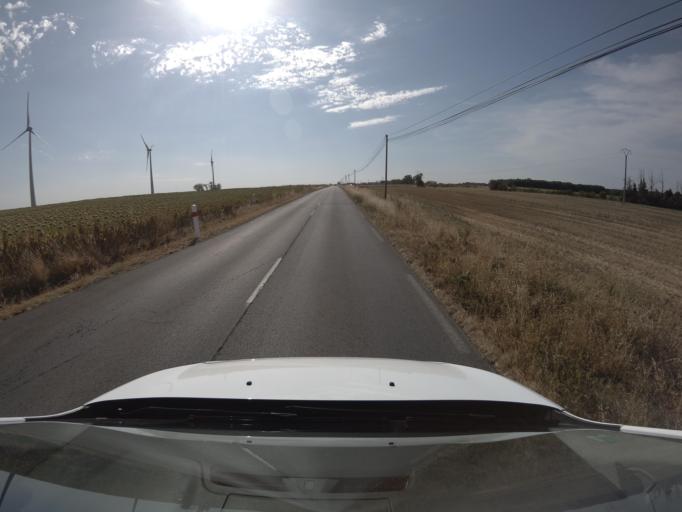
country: FR
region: Poitou-Charentes
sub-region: Departement des Deux-Sevres
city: Mauze-Thouarsais
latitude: 46.9986
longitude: -0.2749
